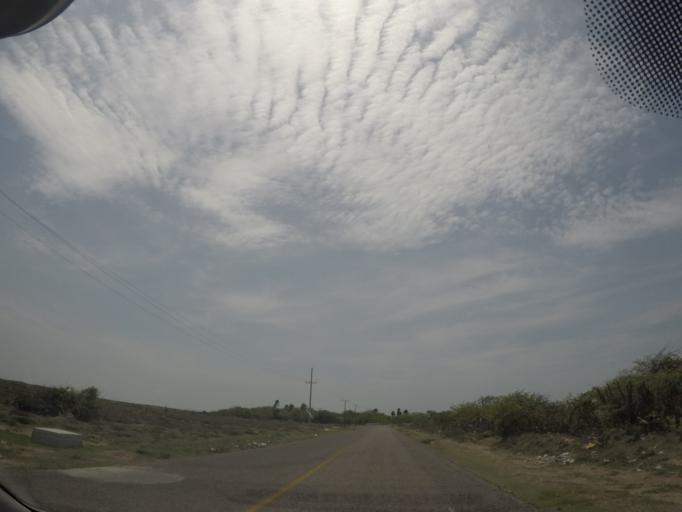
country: MX
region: Oaxaca
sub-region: San Mateo del Mar
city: Colonia Juarez
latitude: 16.2122
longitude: -95.0492
